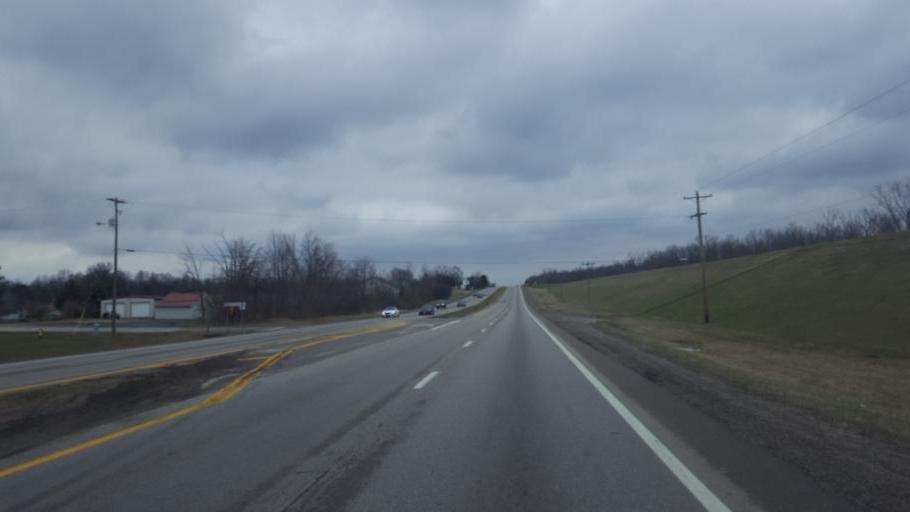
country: US
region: Ohio
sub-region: Delaware County
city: Delaware
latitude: 40.3669
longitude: -83.0737
